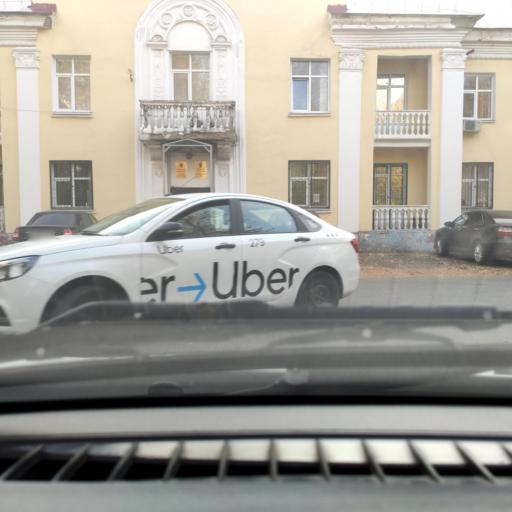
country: RU
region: Samara
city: Tol'yatti
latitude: 53.5116
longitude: 49.4069
